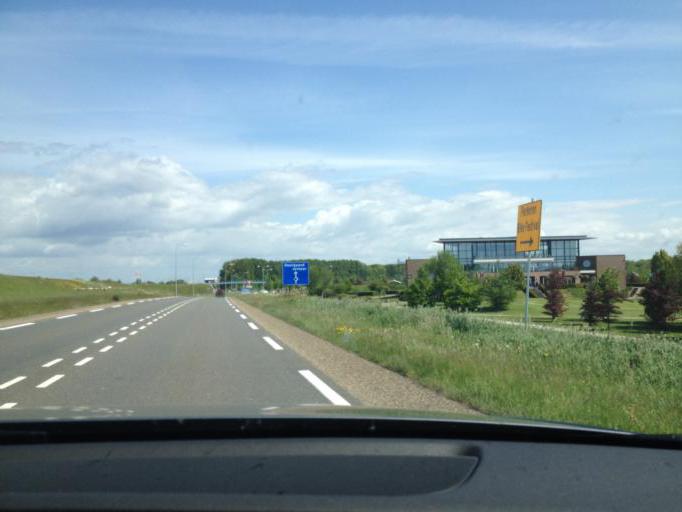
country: NL
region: Flevoland
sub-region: Gemeente Lelystad
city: Lelystad
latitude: 52.5427
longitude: 5.4532
